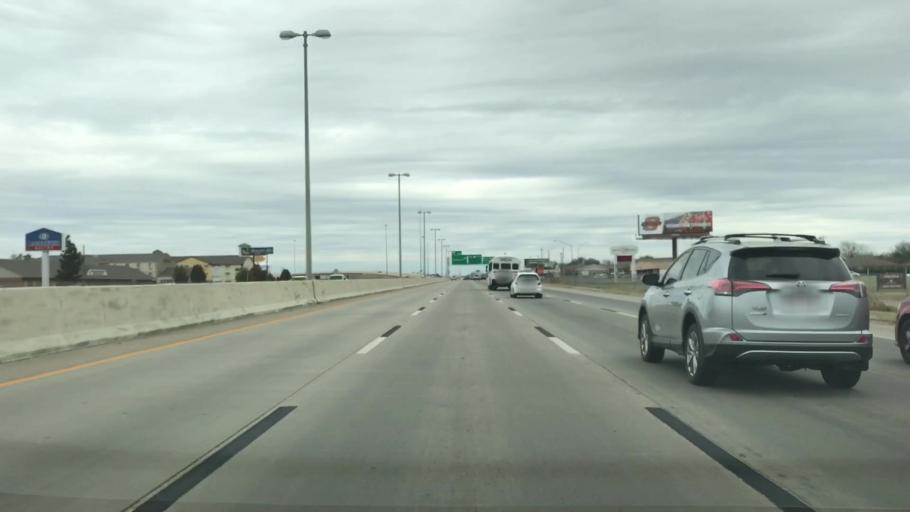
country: US
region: Oklahoma
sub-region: Cleveland County
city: Moore
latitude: 35.3507
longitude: -97.4946
